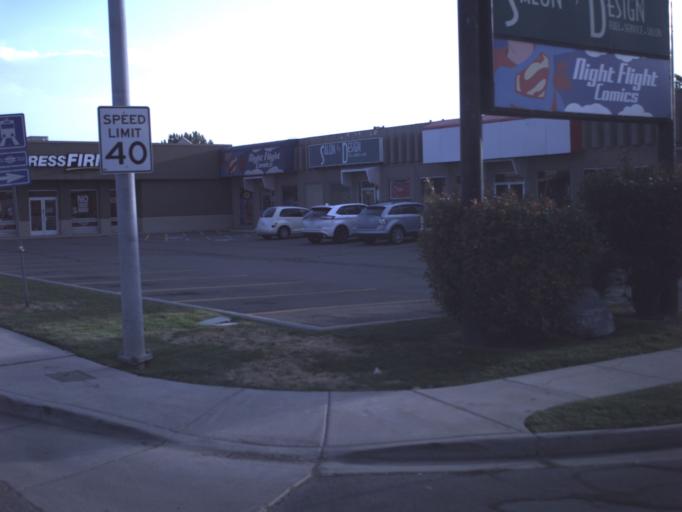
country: US
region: Utah
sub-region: Salt Lake County
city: Midvale
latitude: 40.6360
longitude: -111.8894
